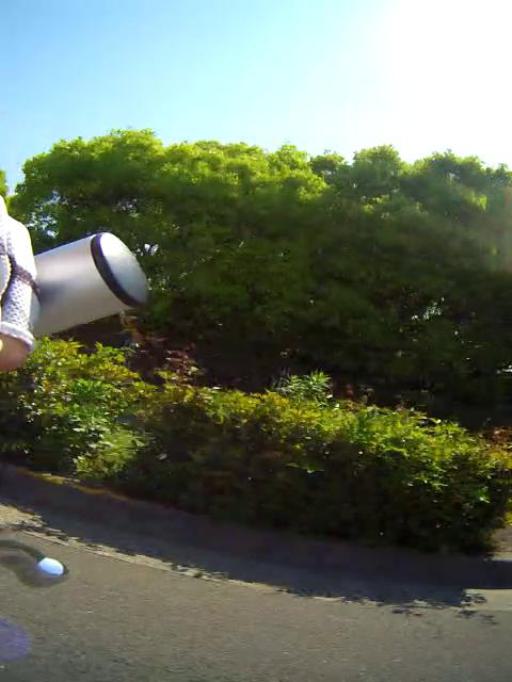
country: JP
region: Osaka
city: Yao
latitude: 34.6346
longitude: 135.5494
